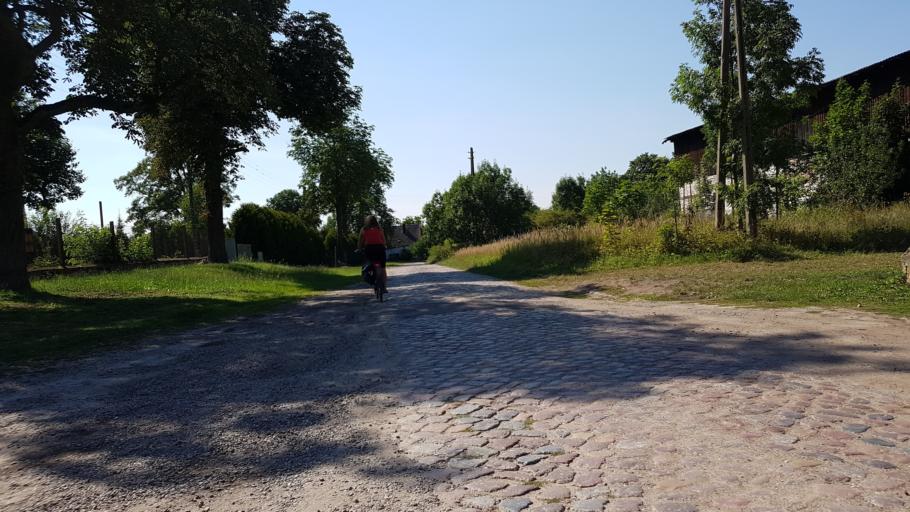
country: PL
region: West Pomeranian Voivodeship
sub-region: Powiat gryfinski
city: Gryfino
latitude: 53.1484
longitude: 14.5077
